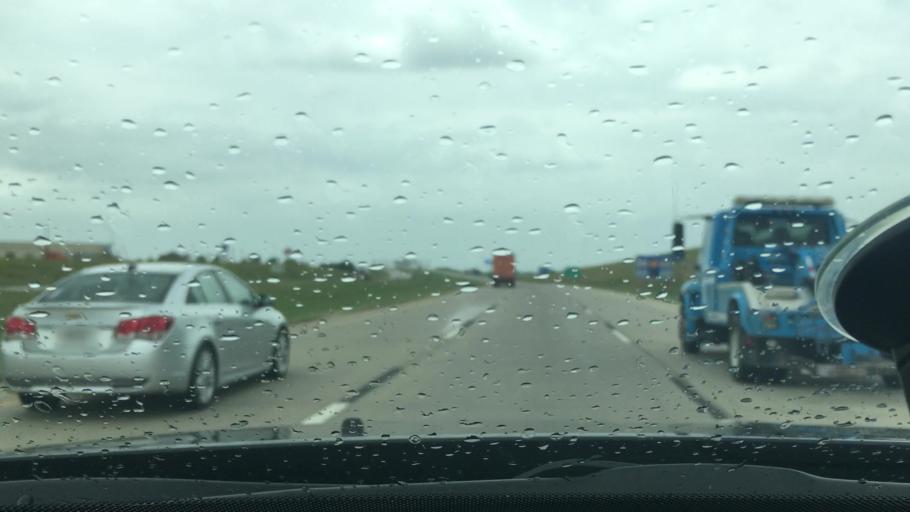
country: US
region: Oklahoma
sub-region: Carter County
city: Ardmore
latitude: 34.1863
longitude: -97.1672
